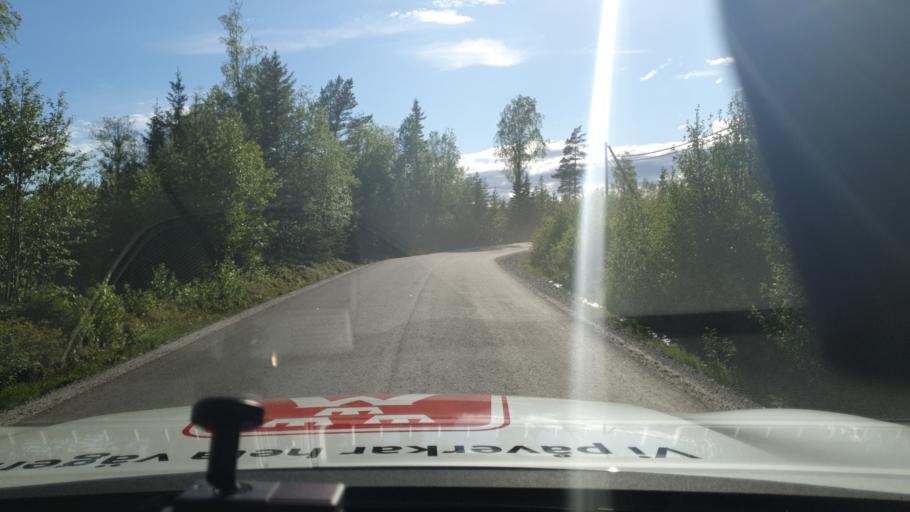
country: SE
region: Vaesterbotten
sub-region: Umea Kommun
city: Taftea
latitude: 63.7648
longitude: 20.4329
